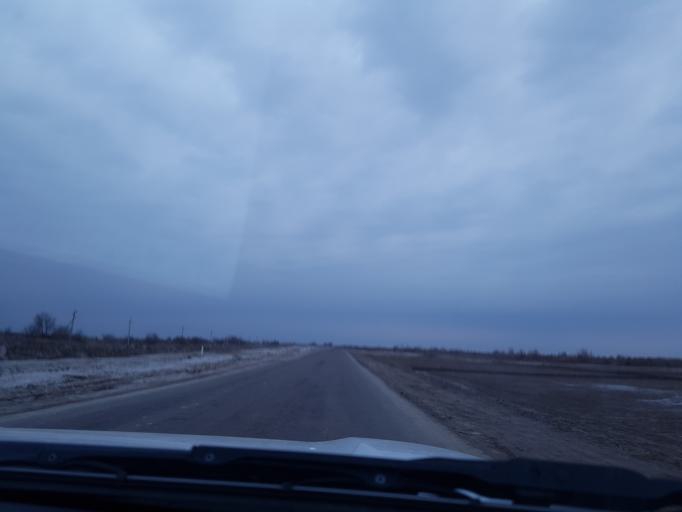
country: TM
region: Dasoguz
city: Yylanly
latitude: 41.9382
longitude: 59.5438
